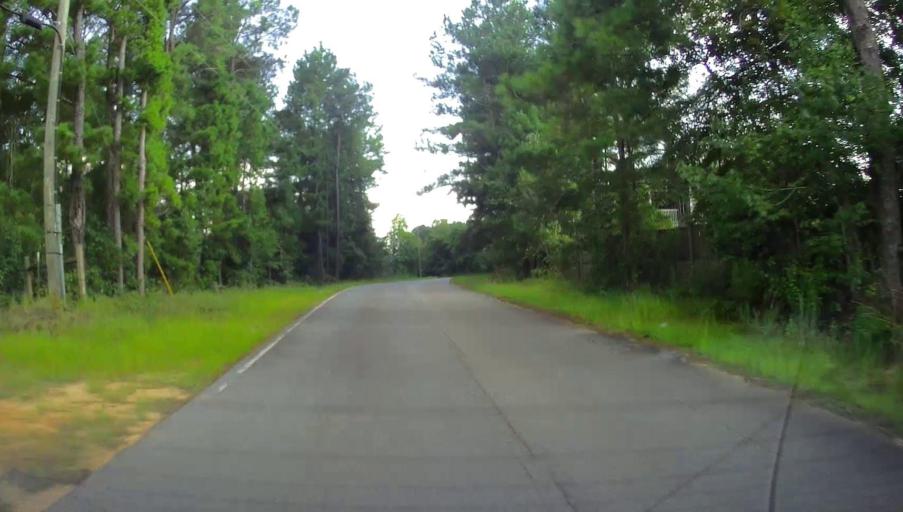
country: US
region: Georgia
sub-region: Houston County
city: Centerville
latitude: 32.5866
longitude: -83.6525
